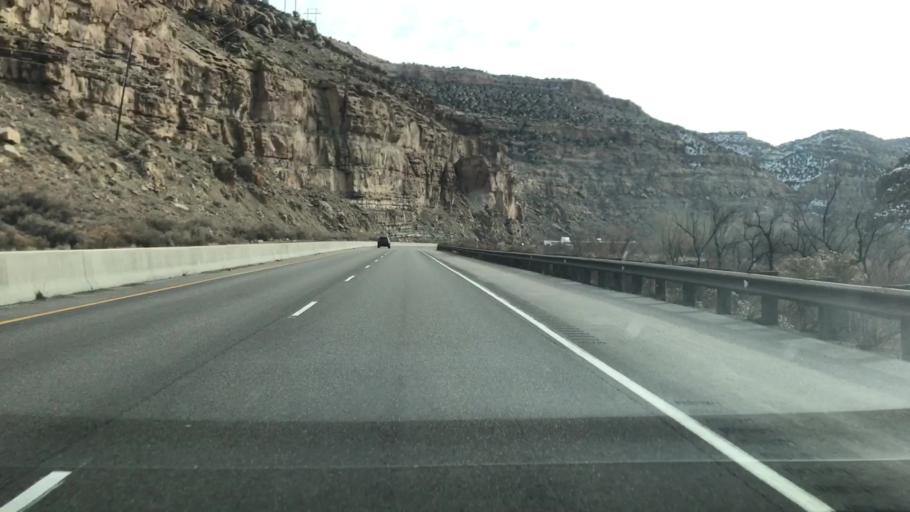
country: US
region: Colorado
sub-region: Mesa County
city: Palisade
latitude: 39.2301
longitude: -108.2683
